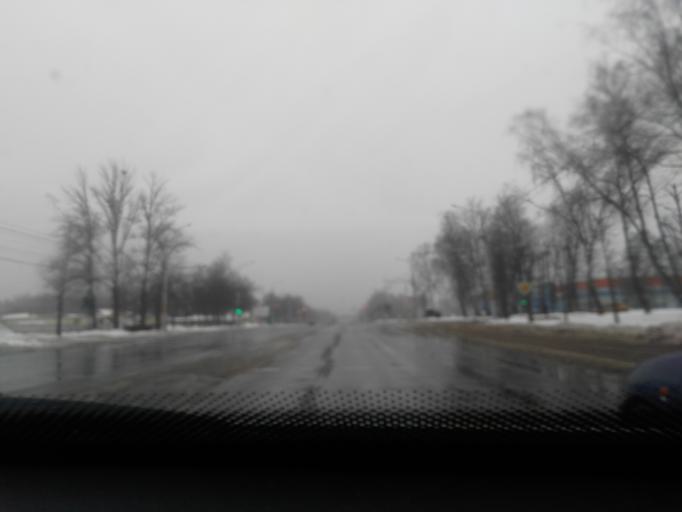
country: BY
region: Mogilev
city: Babruysk
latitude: 53.1719
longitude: 29.2033
